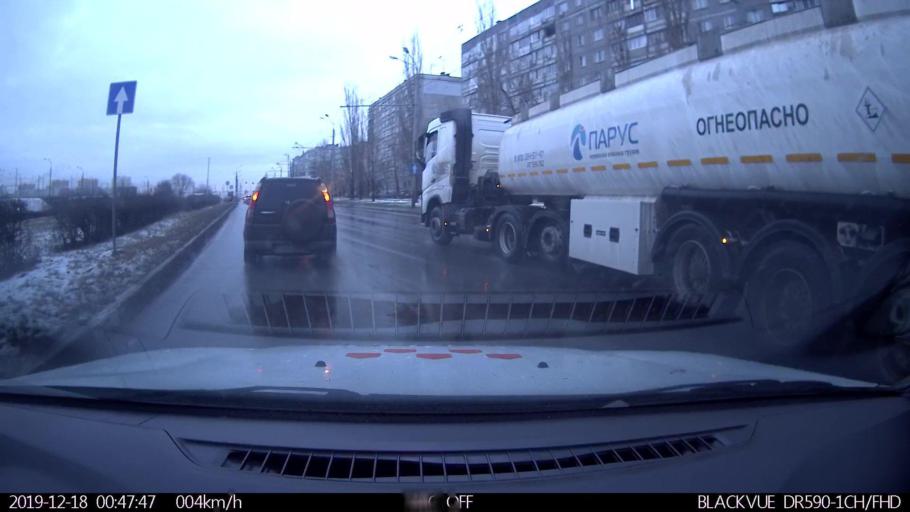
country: RU
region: Nizjnij Novgorod
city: Nizhniy Novgorod
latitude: 56.3379
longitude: 43.9254
